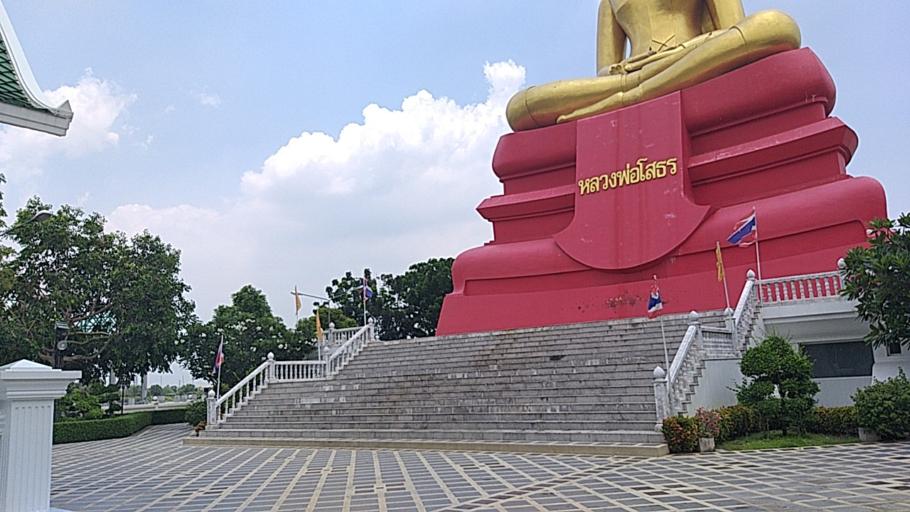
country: TH
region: Pathum Thani
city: Sam Khok
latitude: 14.1148
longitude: 100.5410
